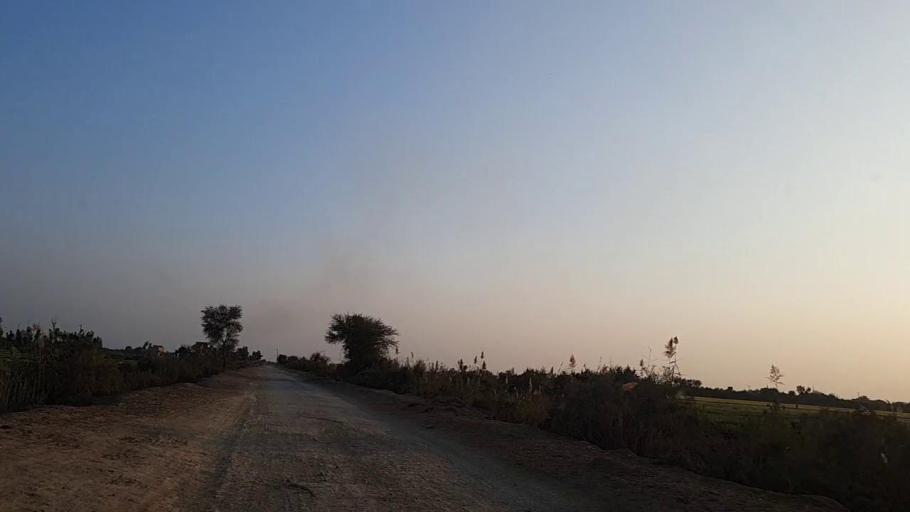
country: PK
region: Sindh
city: Shahdadpur
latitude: 25.9717
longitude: 68.4981
